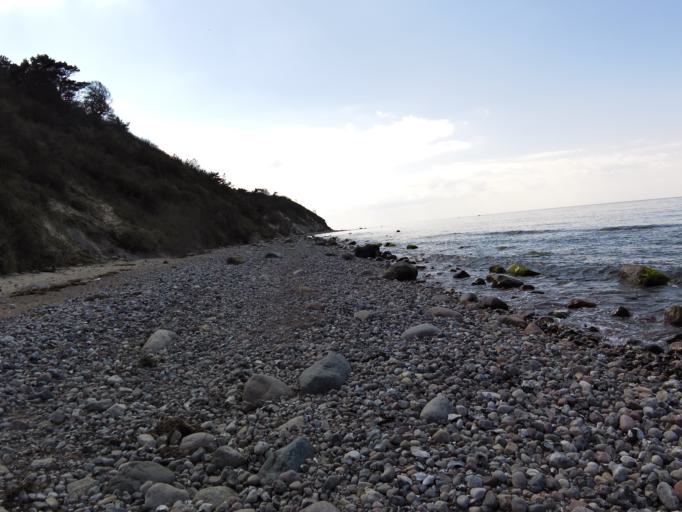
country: DE
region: Mecklenburg-Vorpommern
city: Hiddensee
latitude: 54.5984
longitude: 13.1122
